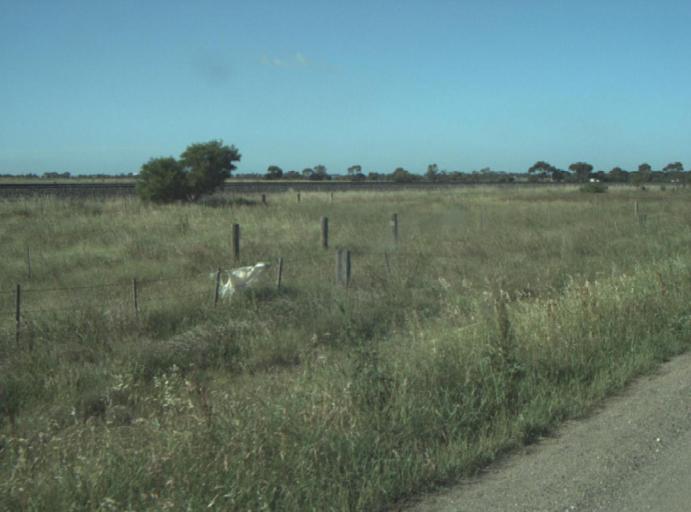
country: AU
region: Victoria
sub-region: Wyndham
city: Little River
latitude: -37.9922
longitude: 144.4531
